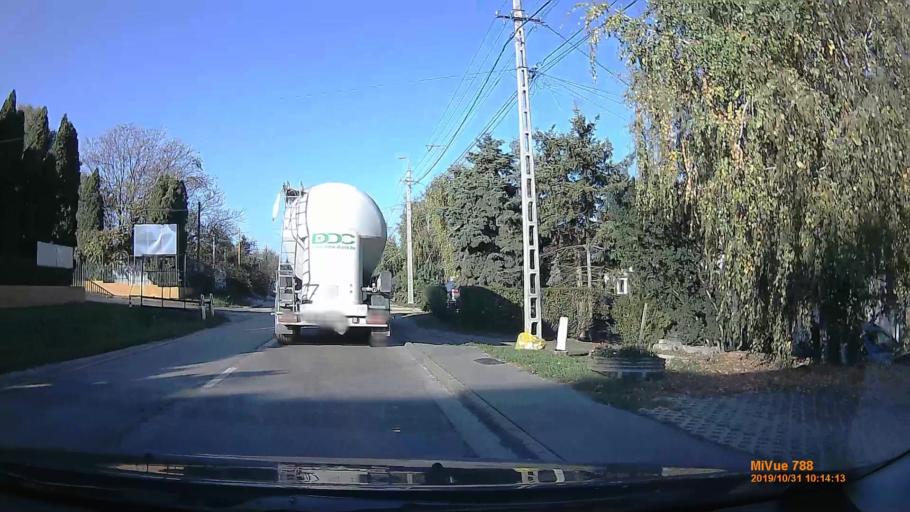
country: HU
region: Pest
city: Pecel
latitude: 47.4919
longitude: 19.3198
